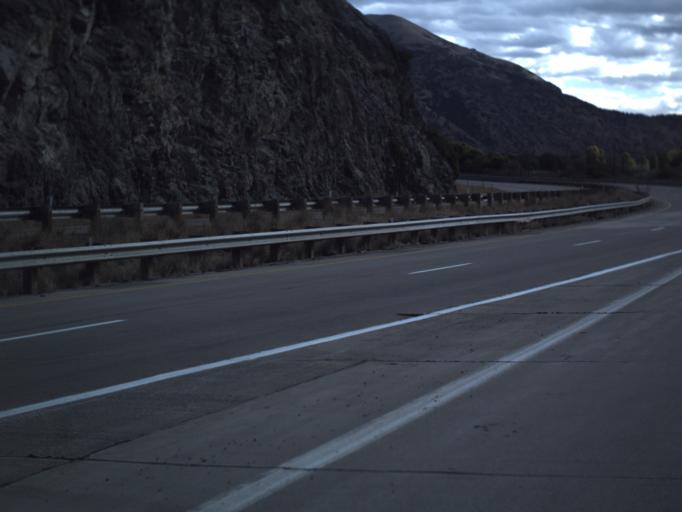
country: US
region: Utah
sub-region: Morgan County
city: Morgan
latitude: 41.0412
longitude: -111.6618
